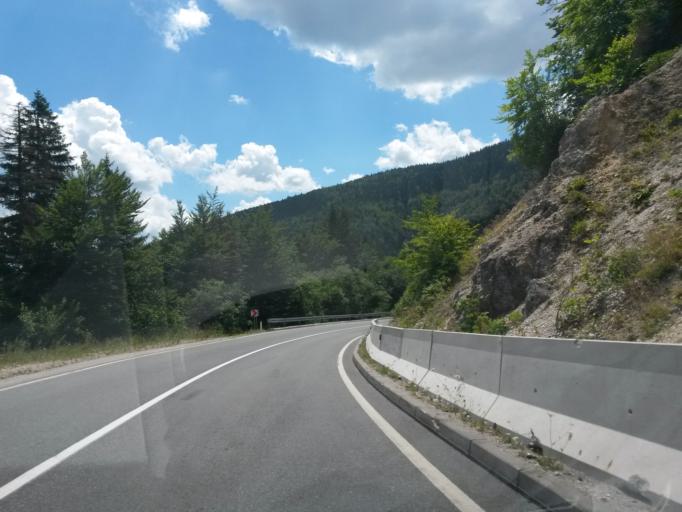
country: BA
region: Federation of Bosnia and Herzegovina
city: Bugojno
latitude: 44.0256
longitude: 17.3017
